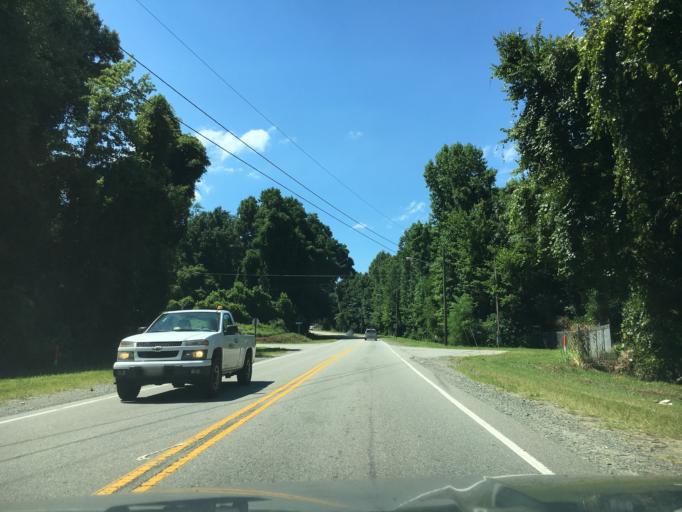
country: US
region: Virginia
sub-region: Halifax County
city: South Boston
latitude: 36.7164
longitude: -78.8986
